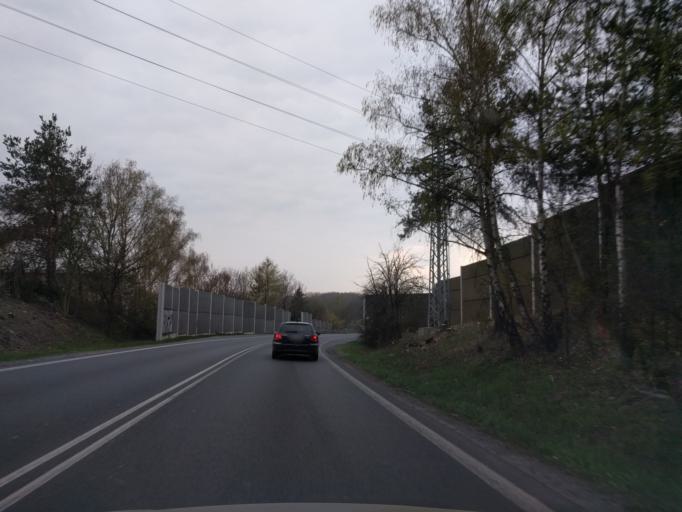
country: CZ
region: Central Bohemia
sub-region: Okres Praha-Vychod
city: Ricany
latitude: 49.9811
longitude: 14.6364
